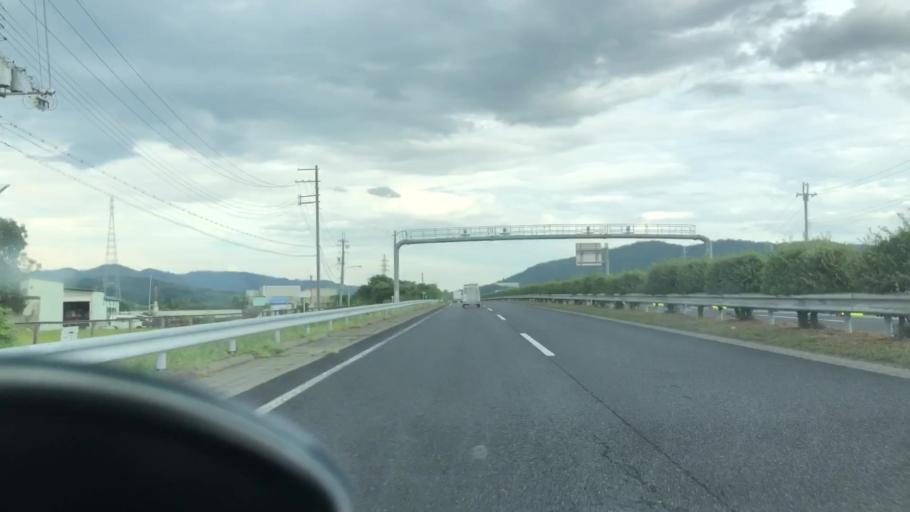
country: JP
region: Hyogo
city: Himeji
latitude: 34.9479
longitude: 134.7698
